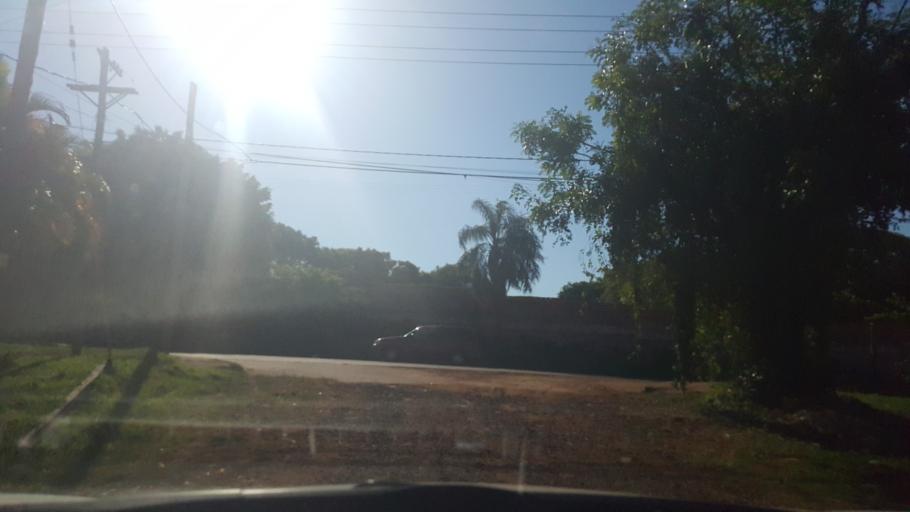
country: AR
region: Misiones
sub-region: Departamento de Capital
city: Posadas
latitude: -27.3823
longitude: -55.9107
